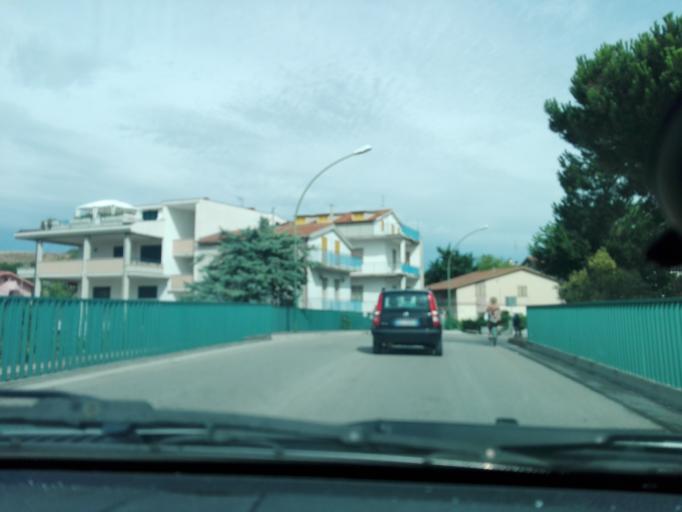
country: IT
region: Abruzzo
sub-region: Provincia di Teramo
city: Pineto
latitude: 42.6104
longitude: 14.0629
